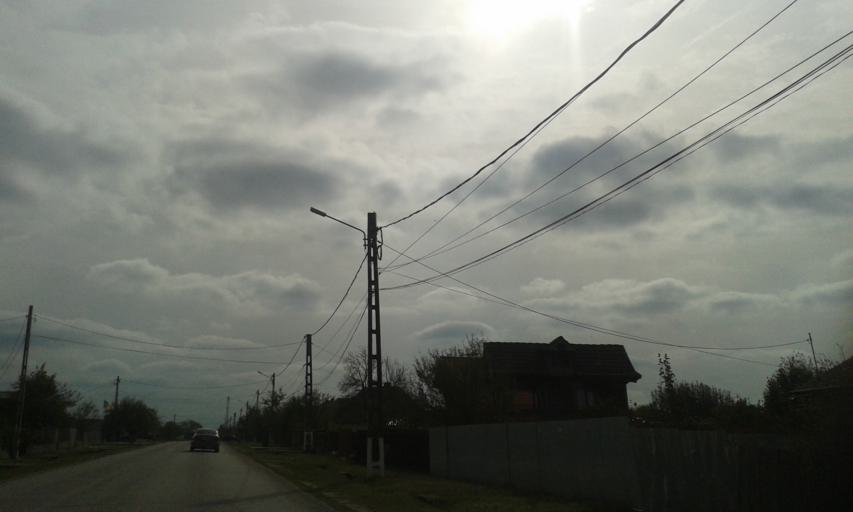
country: RO
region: Gorj
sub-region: Comuna Targu Carbunesti
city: Pojogeni
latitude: 44.9981
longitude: 23.4925
